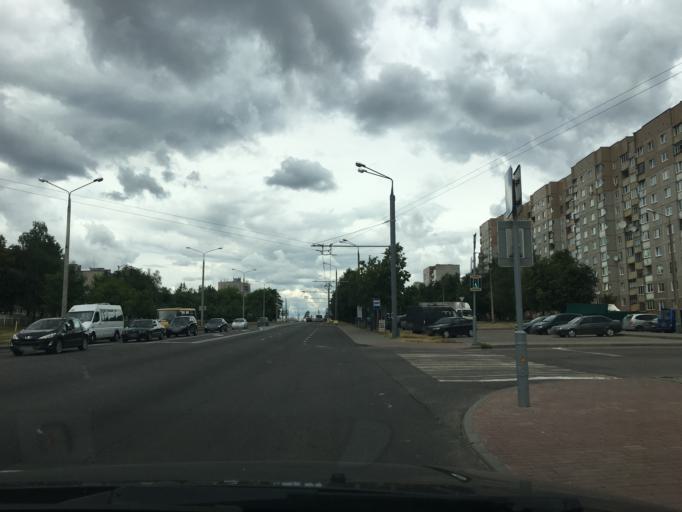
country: BY
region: Grodnenskaya
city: Hrodna
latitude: 53.6444
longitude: 23.8399
